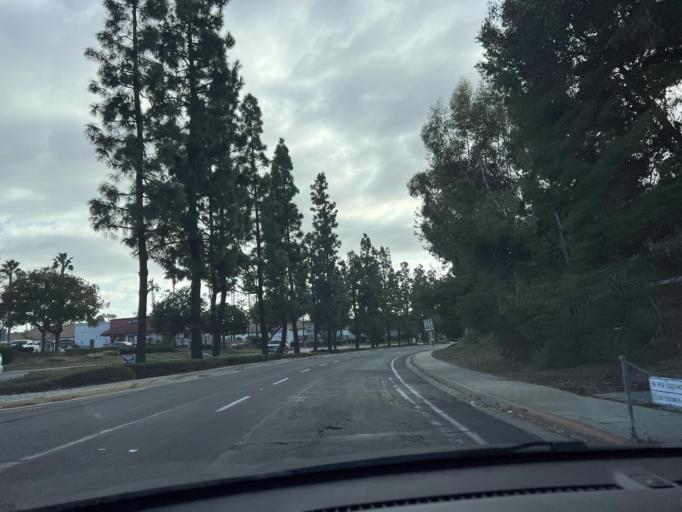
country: US
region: California
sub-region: San Diego County
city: Fairbanks Ranch
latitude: 32.9595
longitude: -117.1265
